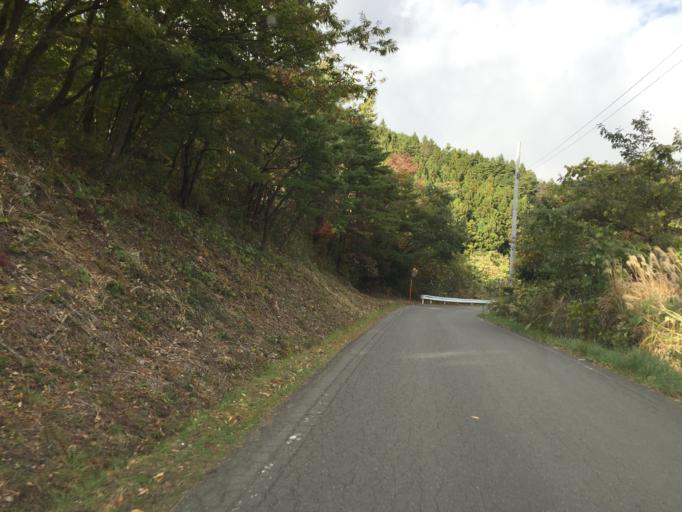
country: JP
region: Fukushima
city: Fukushima-shi
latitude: 37.7152
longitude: 140.3433
